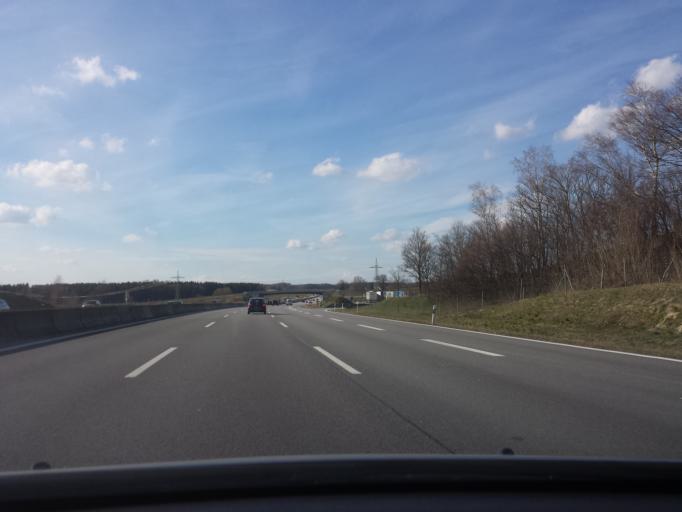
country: DE
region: Bavaria
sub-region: Upper Bavaria
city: Sulzemoos
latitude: 48.2571
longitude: 11.3020
